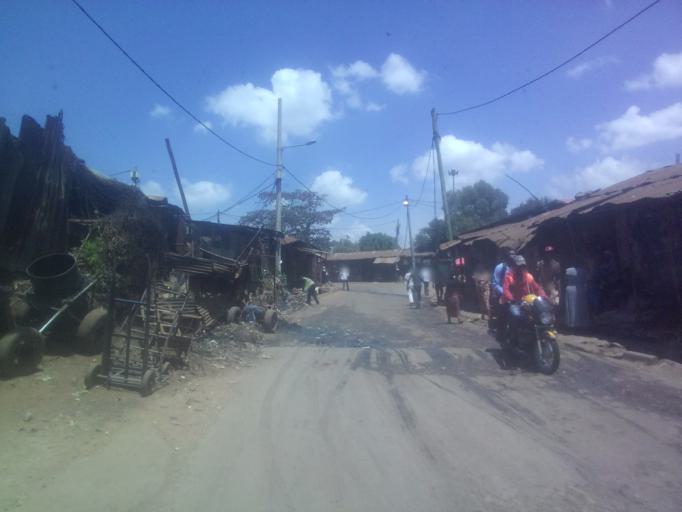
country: KE
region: Nairobi Area
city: Nairobi
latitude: -1.3100
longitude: 36.7869
